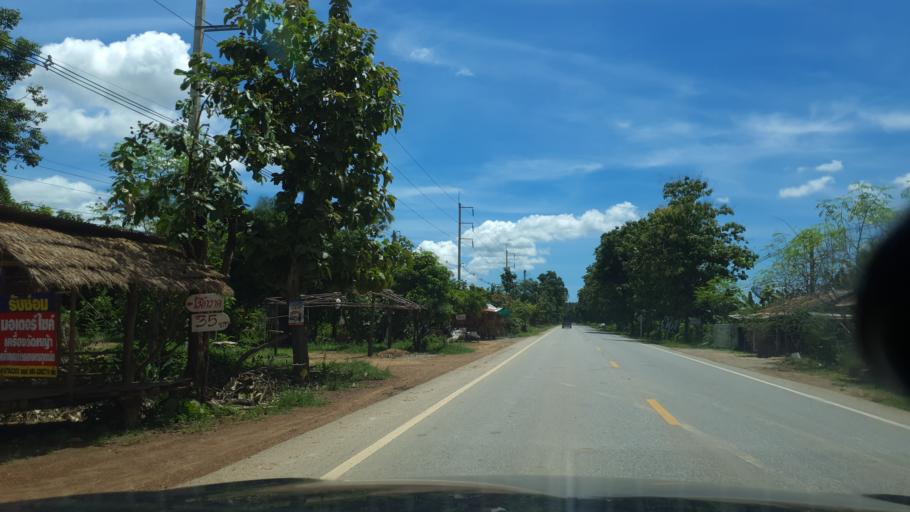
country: TH
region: Sukhothai
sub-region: Amphoe Si Satchanalai
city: Si Satchanalai
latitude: 17.4574
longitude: 99.7863
